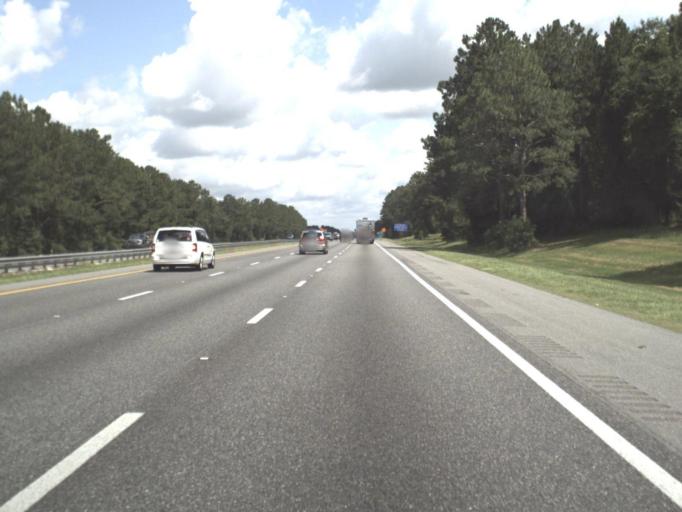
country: US
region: Florida
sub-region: Columbia County
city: Lake City
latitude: 30.0980
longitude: -82.6443
